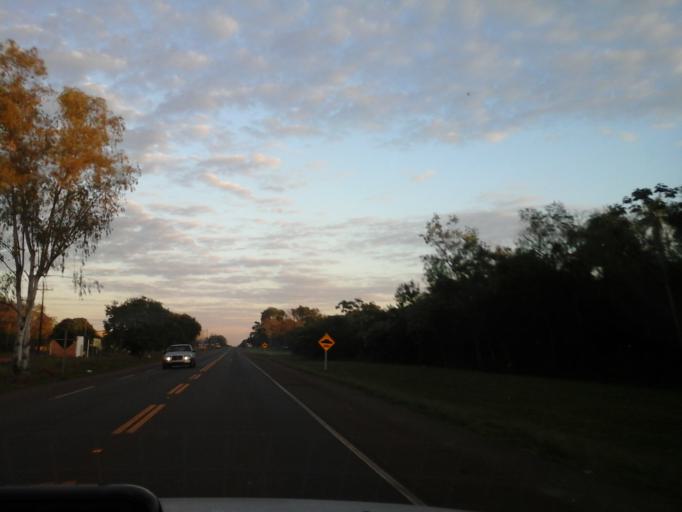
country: PY
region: Misiones
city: Santiago
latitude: -27.0461
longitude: -56.6493
